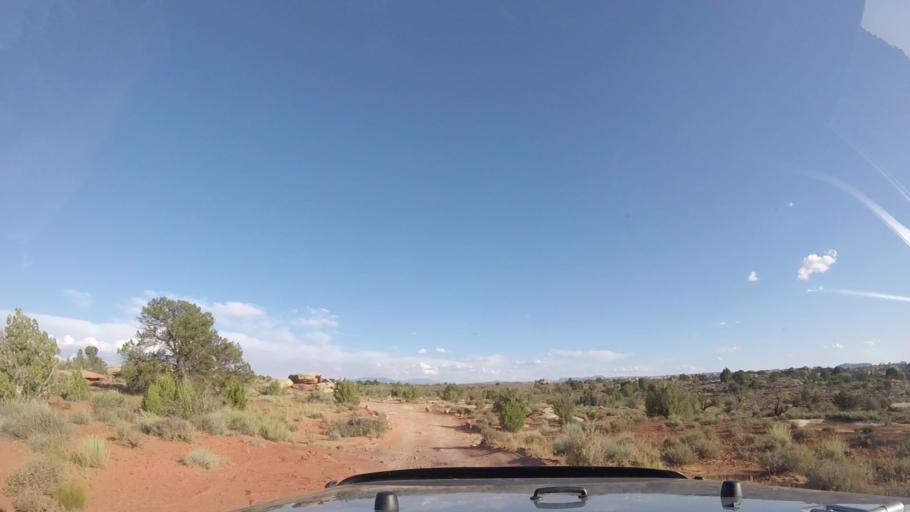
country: US
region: Utah
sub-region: Grand County
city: Moab
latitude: 38.2092
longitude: -109.7876
